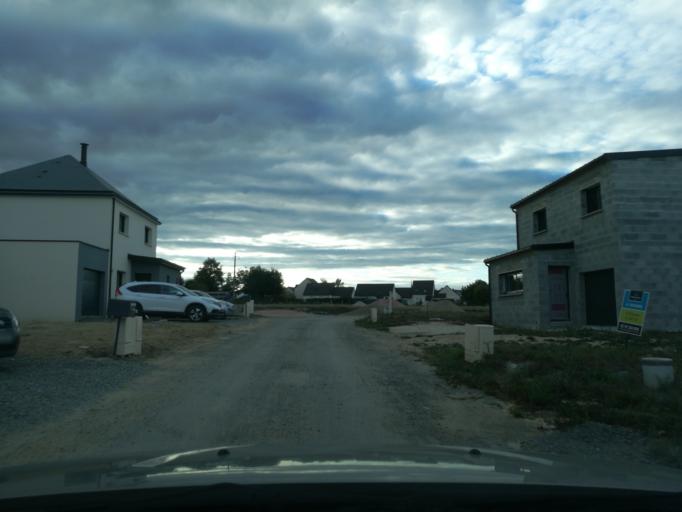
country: FR
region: Brittany
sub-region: Departement d'Ille-et-Vilaine
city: Bedee
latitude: 48.1751
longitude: -1.9343
